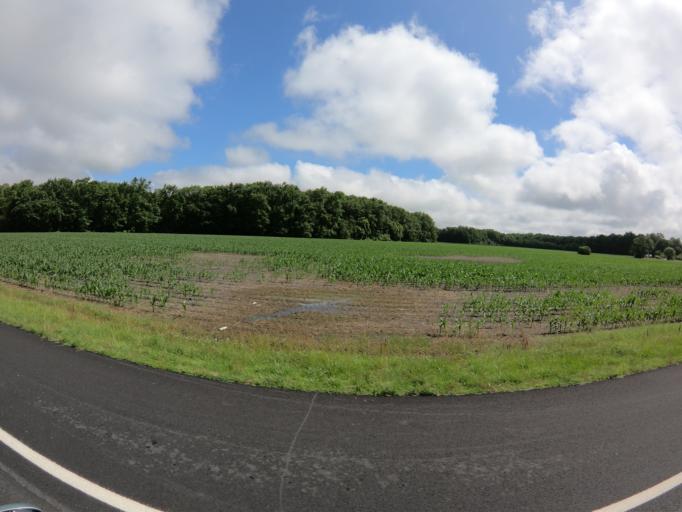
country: US
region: Maryland
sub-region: Caroline County
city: Greensboro
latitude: 39.0402
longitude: -75.8008
